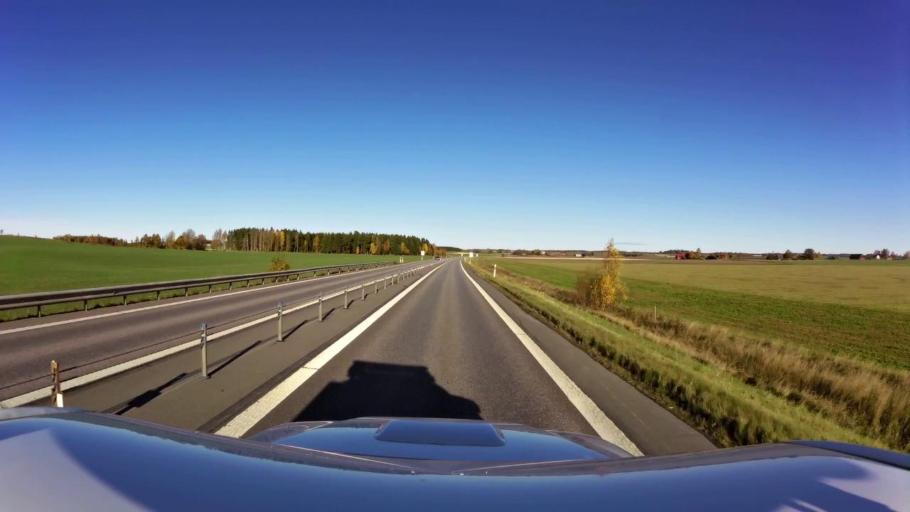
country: SE
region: OEstergoetland
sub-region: Linkopings Kommun
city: Berg
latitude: 58.4542
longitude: 15.5029
